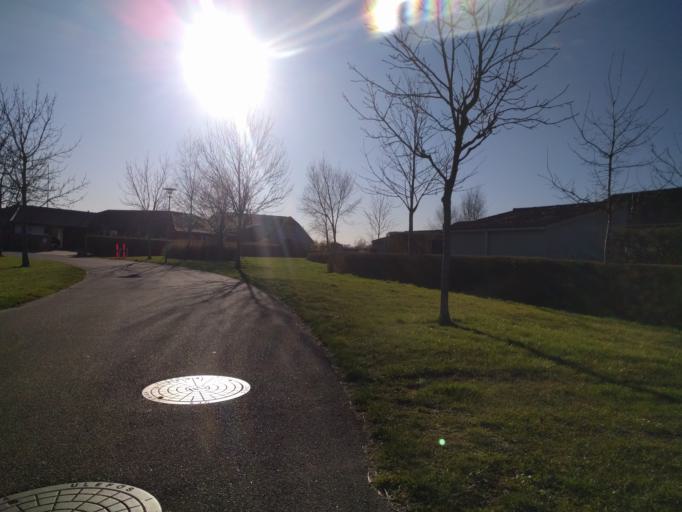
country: DK
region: South Denmark
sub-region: Odense Kommune
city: Bullerup
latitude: 55.3886
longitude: 10.5214
